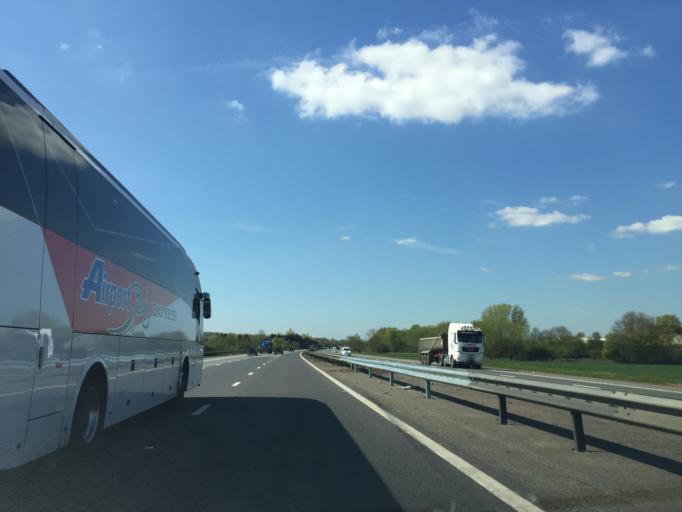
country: GB
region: England
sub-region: Essex
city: Theydon Bois
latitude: 51.6505
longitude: 0.0995
